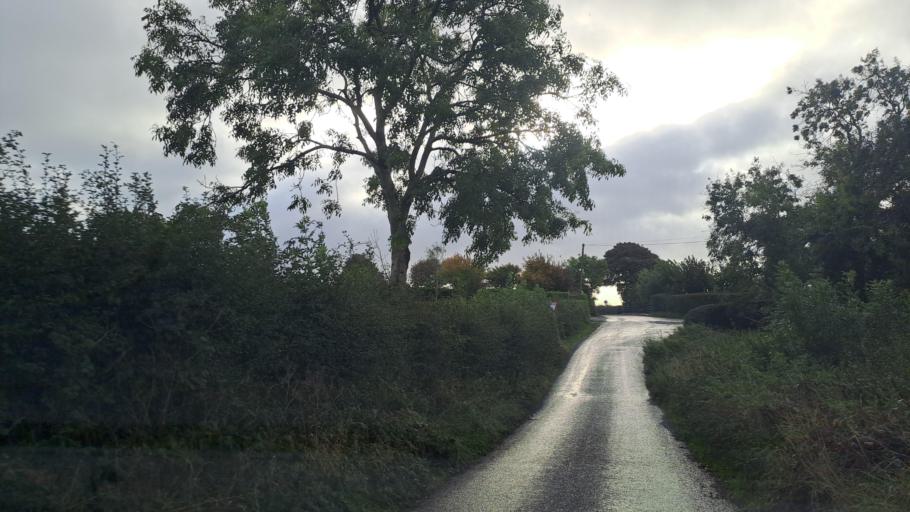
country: IE
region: Ulster
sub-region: An Cabhan
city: Kingscourt
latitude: 53.9606
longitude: -6.8185
